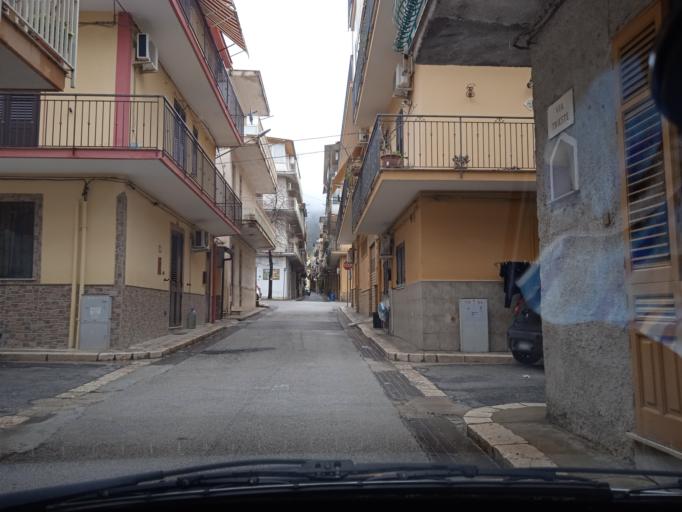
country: IT
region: Sicily
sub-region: Palermo
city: Villabate
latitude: 38.0792
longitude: 13.4449
